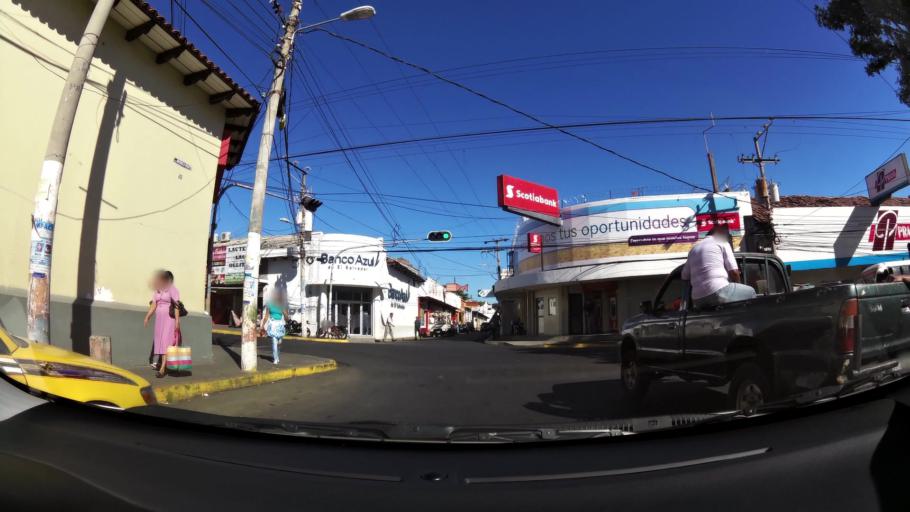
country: SV
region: San Miguel
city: San Miguel
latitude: 13.4831
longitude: -88.1759
